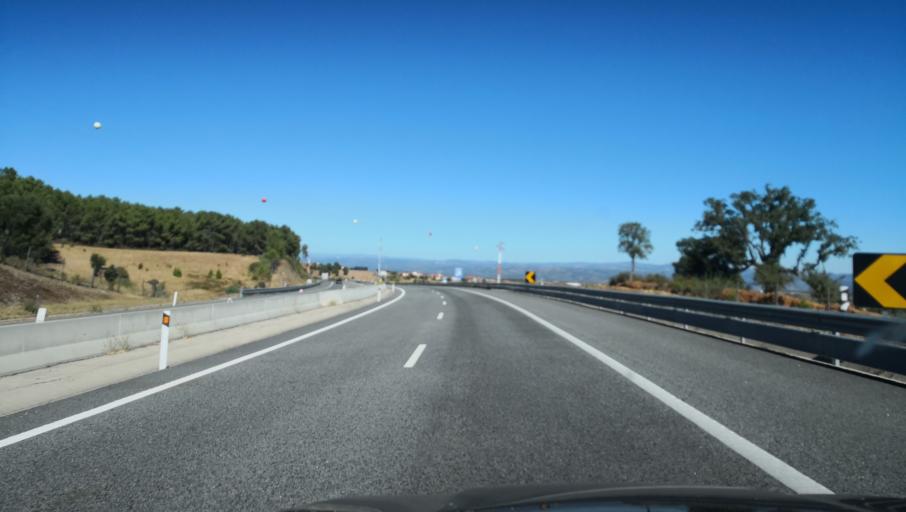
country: PT
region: Braganca
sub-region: Mirandela
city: Mirandela
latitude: 41.4533
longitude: -7.2677
